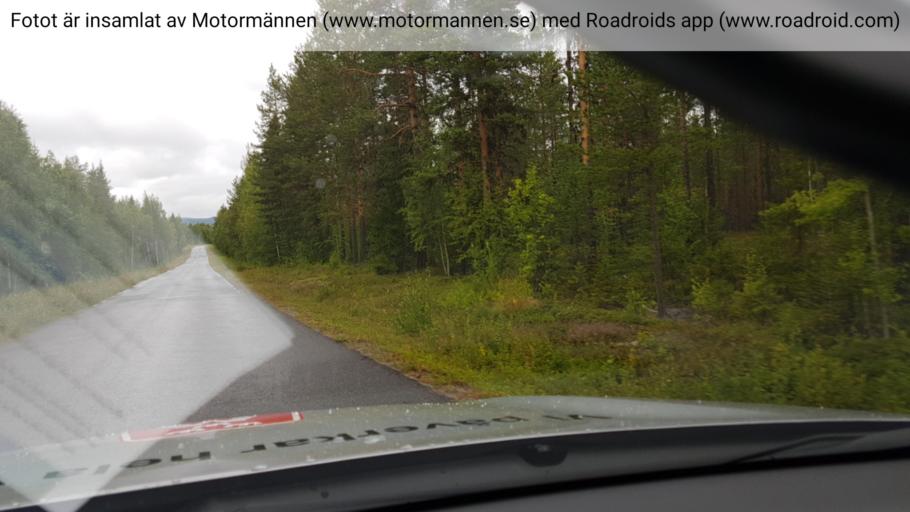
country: SE
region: Norrbotten
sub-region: Alvsbyns Kommun
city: AElvsbyn
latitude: 66.0787
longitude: 20.9138
